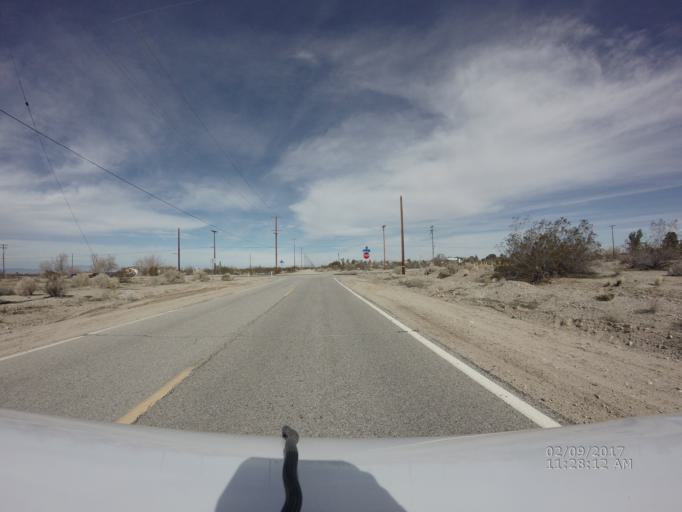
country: US
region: California
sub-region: Los Angeles County
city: Littlerock
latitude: 34.5423
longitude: -117.9229
